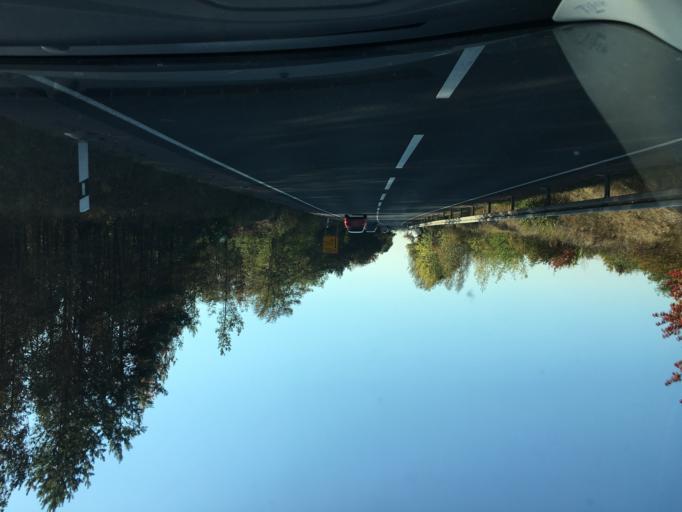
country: DE
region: Saxony-Anhalt
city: Roitzsch
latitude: 51.5718
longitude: 12.2840
